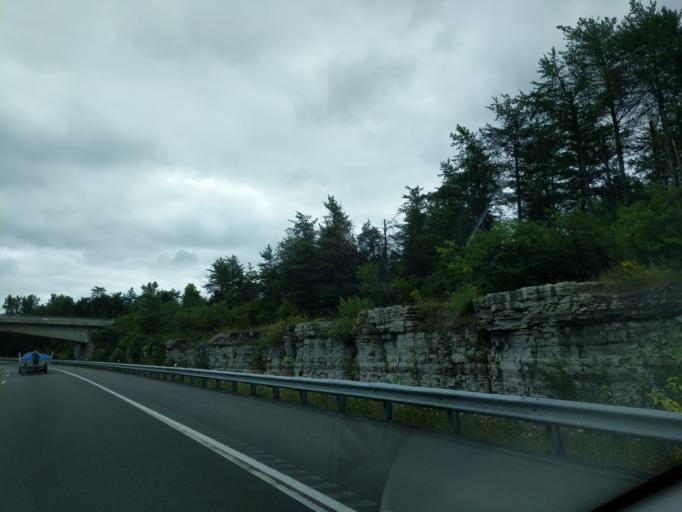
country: CA
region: Ontario
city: Bells Corners
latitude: 45.2958
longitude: -75.7941
